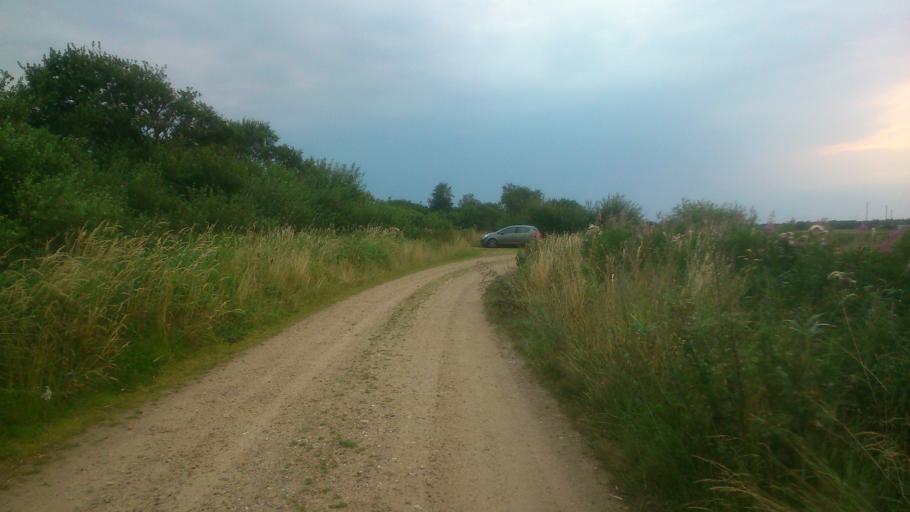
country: DK
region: Central Jutland
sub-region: Ringkobing-Skjern Kommune
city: Tarm
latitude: 55.9298
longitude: 8.5228
